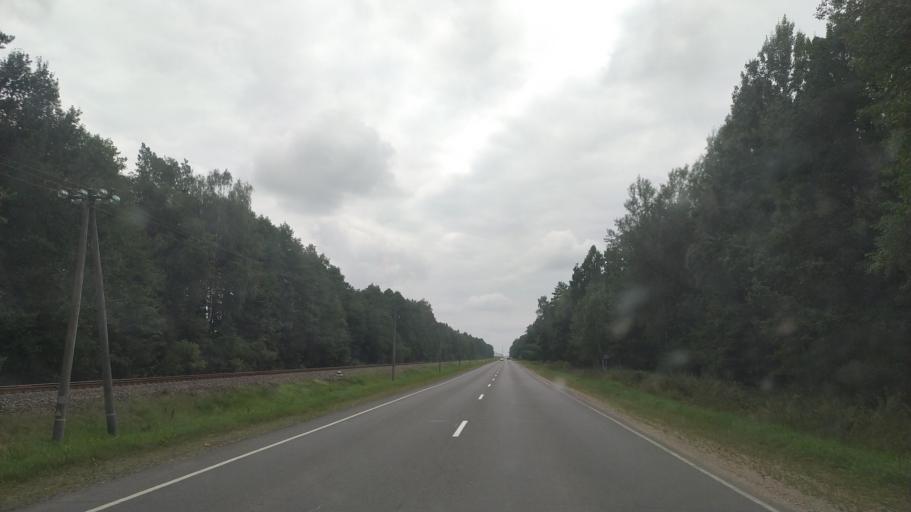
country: BY
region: Brest
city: Byelaazyorsk
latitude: 52.5343
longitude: 25.1418
